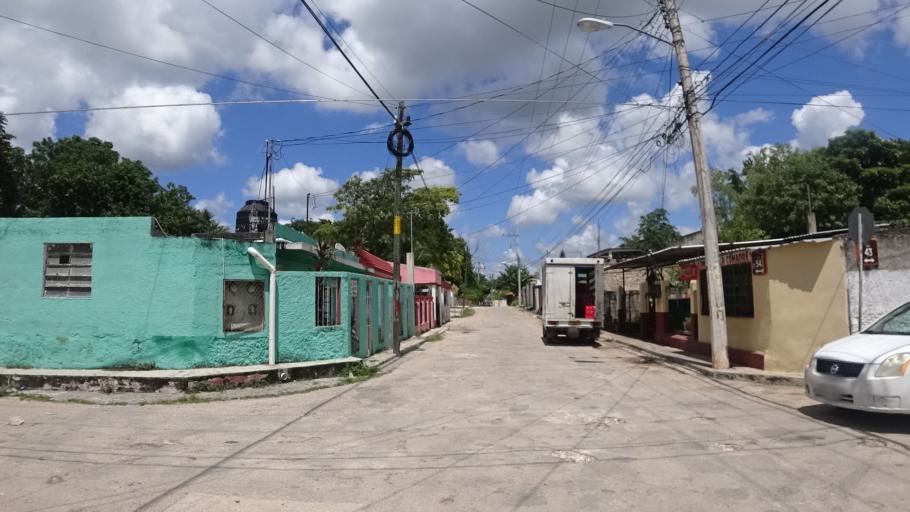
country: MX
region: Yucatan
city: Valladolid
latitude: 20.6883
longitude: -88.2120
